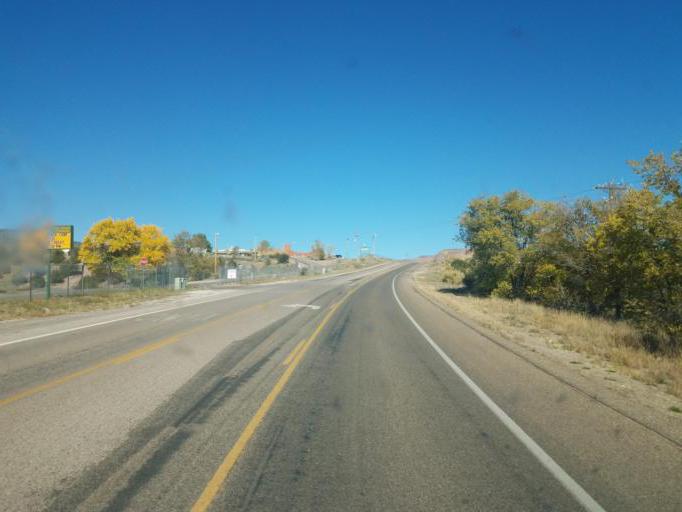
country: US
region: New Mexico
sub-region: Sandoval County
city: Jemez Pueblo
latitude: 35.6560
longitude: -106.7355
